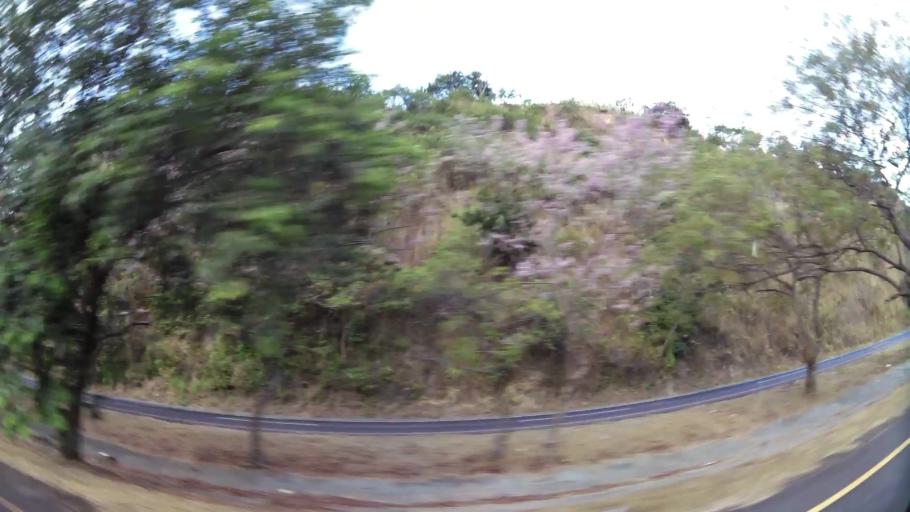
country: SV
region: San Vicente
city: San Vicente
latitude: 13.6685
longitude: -88.8291
